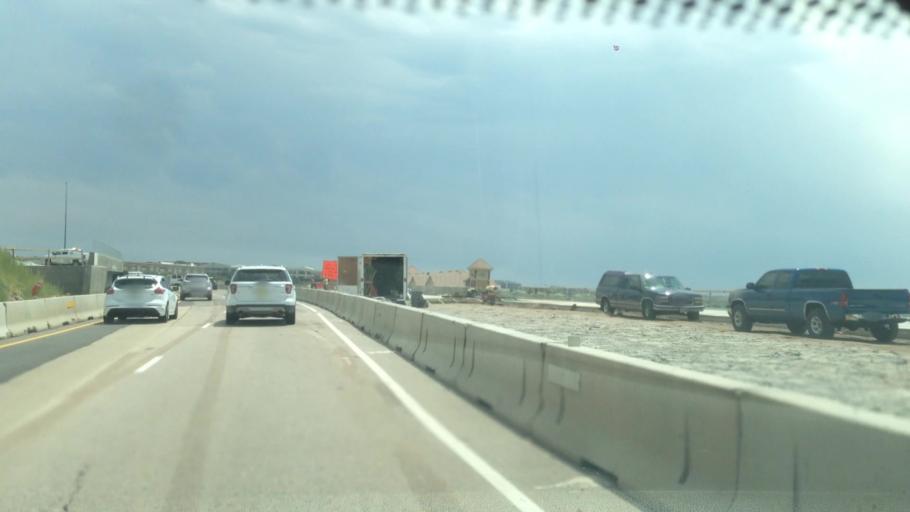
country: US
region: Colorado
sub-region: Adams County
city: Lone Tree
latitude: 39.5590
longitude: -104.8819
